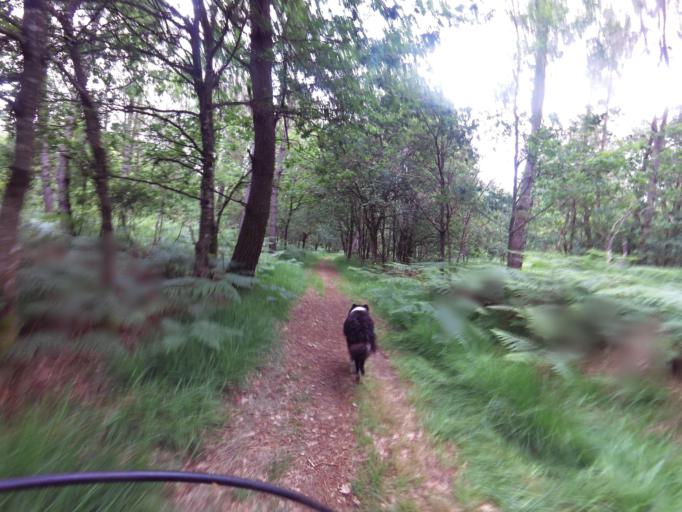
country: FR
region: Brittany
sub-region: Departement du Morbihan
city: Molac
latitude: 47.7586
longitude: -2.4266
